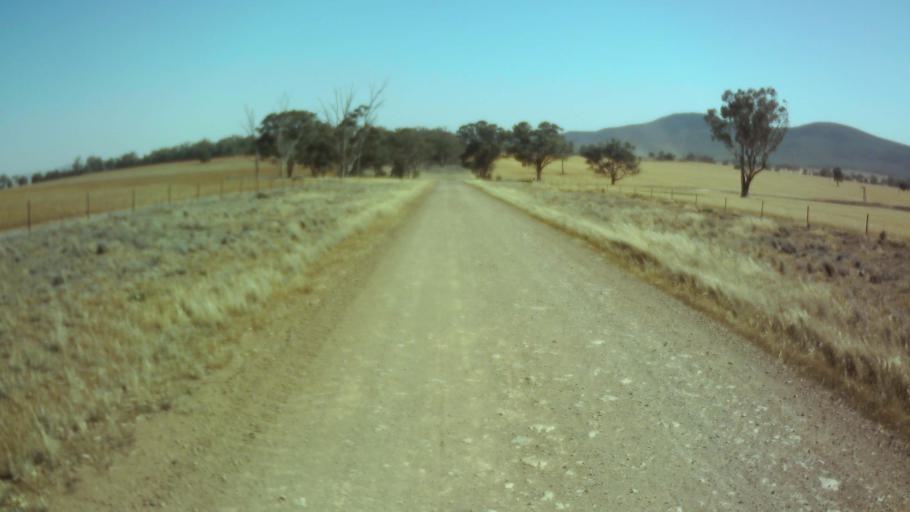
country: AU
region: New South Wales
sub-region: Weddin
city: Grenfell
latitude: -33.8532
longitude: 148.0160
